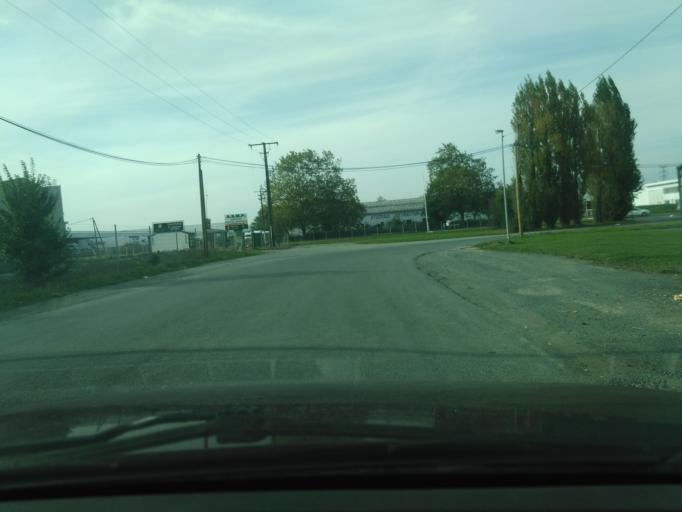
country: FR
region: Pays de la Loire
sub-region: Departement de la Vendee
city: Les Essarts
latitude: 46.7585
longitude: -1.2459
